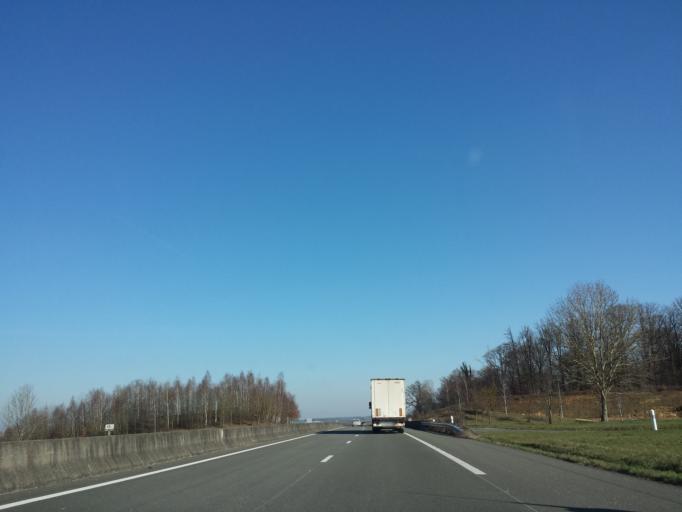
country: FR
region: Picardie
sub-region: Departement de l'Oise
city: Allonne
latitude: 49.3986
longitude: 2.1233
